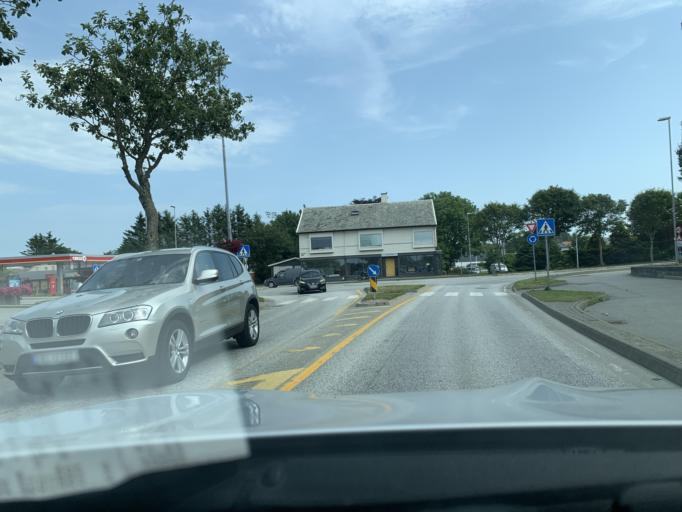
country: NO
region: Rogaland
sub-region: Klepp
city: Kleppe
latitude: 58.7763
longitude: 5.6297
